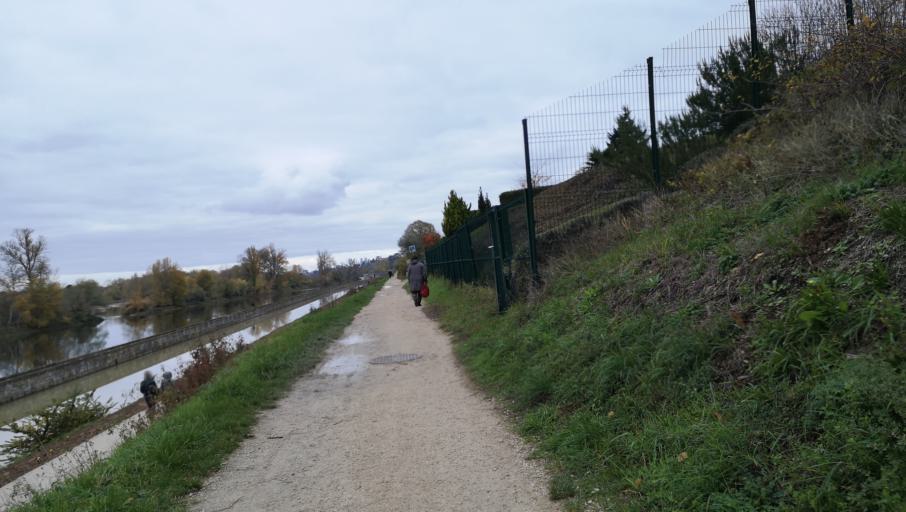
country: FR
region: Centre
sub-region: Departement du Loiret
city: Saint-Jean-de-Braye
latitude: 47.9035
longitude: 1.9700
